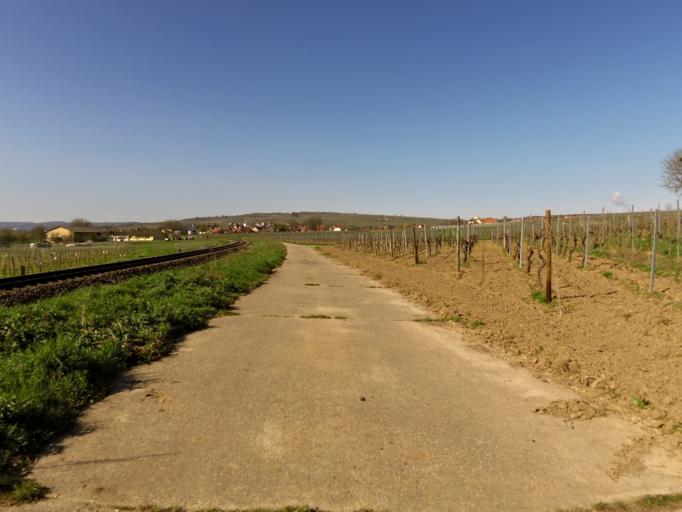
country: DE
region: Rheinland-Pfalz
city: Bockenheim
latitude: 49.6135
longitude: 8.1955
